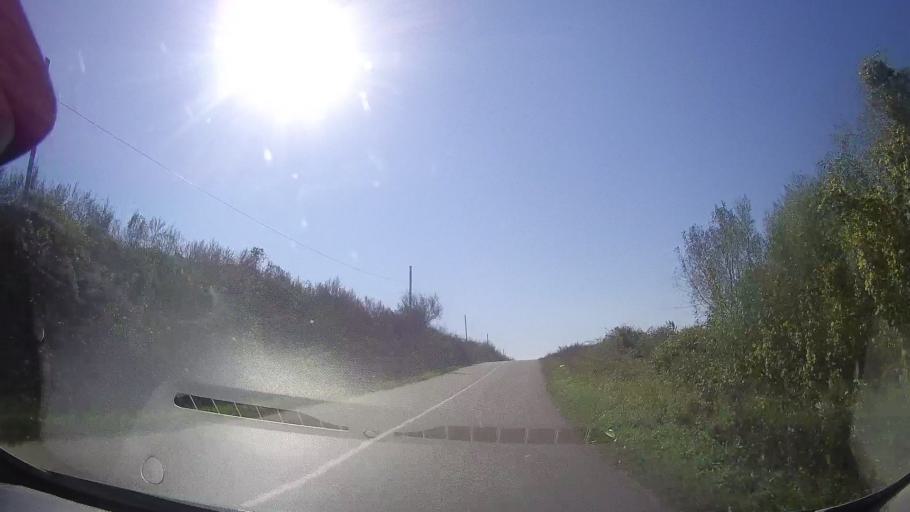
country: RO
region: Timis
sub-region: Comuna Bethausen
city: Bethausen
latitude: 45.8541
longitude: 21.9663
